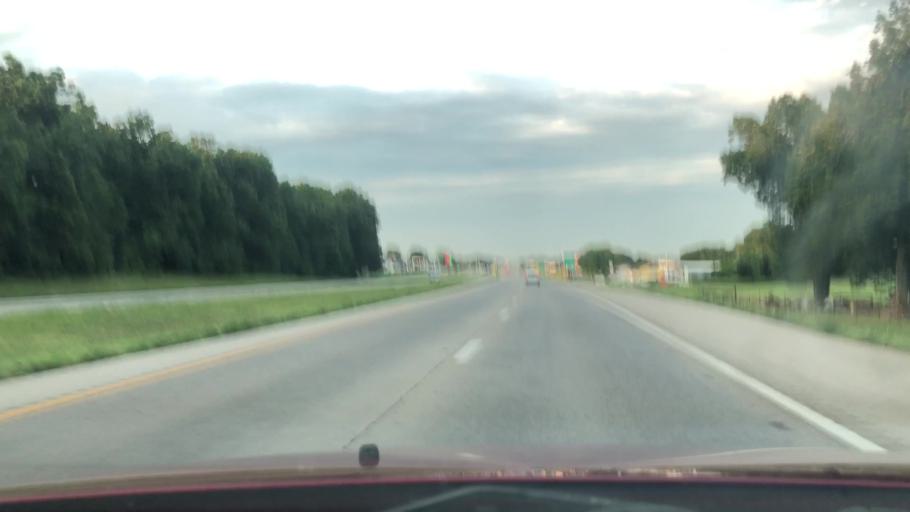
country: US
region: Missouri
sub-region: Greene County
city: Republic
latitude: 37.1426
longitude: -93.4349
